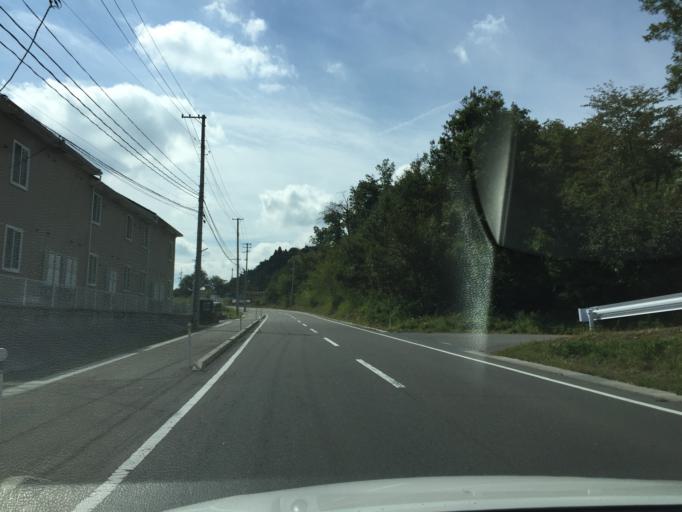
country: JP
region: Fukushima
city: Miharu
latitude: 37.4425
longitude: 140.5184
